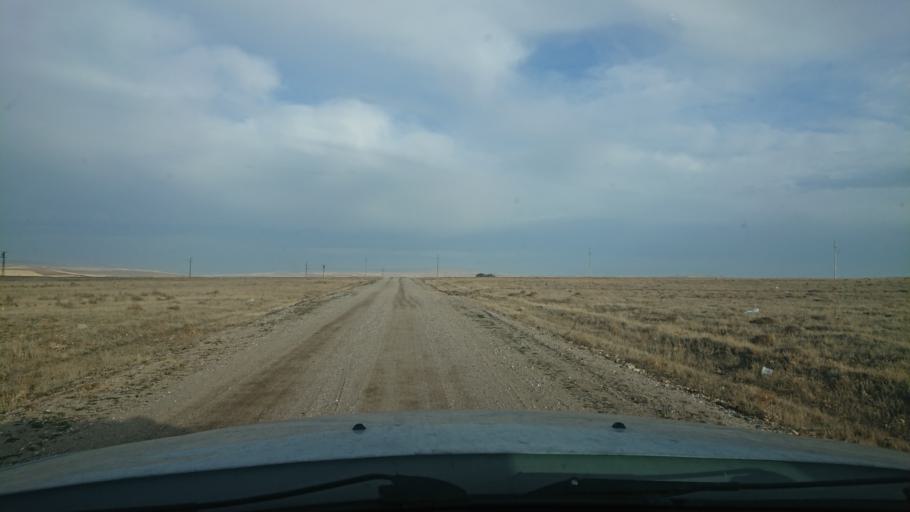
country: TR
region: Aksaray
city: Agacoren
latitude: 38.7173
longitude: 33.8684
